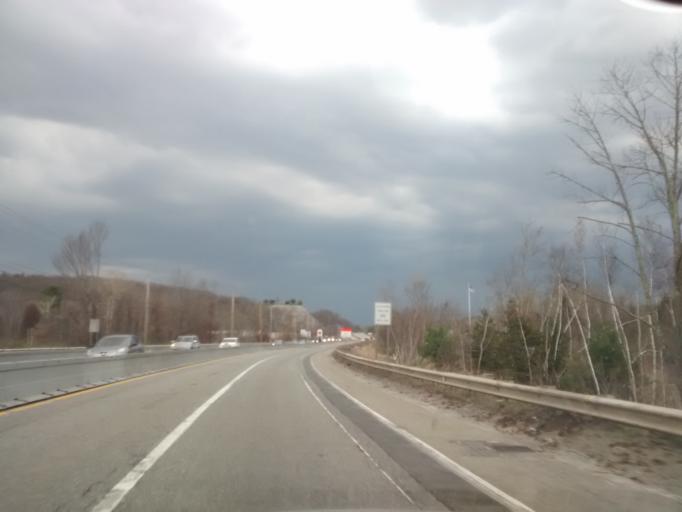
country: US
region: Massachusetts
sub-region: Worcester County
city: Millbury
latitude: 42.1888
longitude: -71.7679
